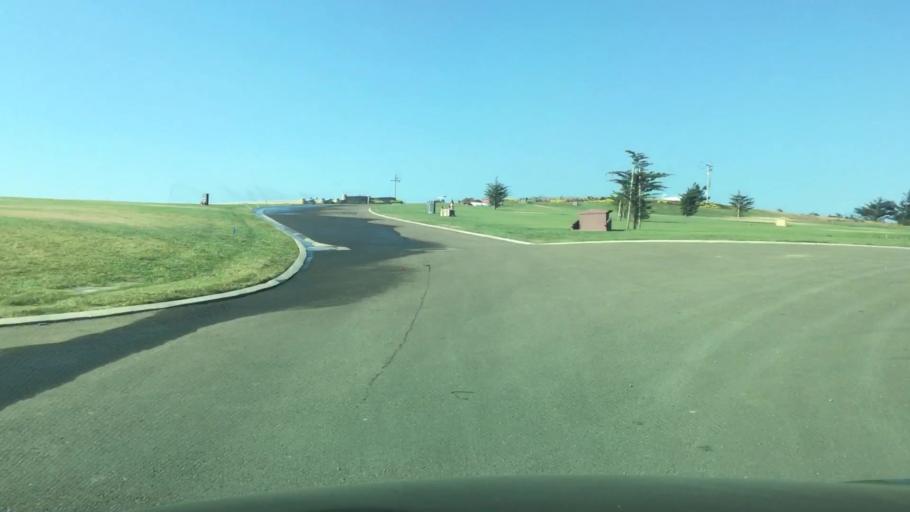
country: US
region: California
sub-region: San Mateo County
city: Highlands-Baywood Park
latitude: 37.5029
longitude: -122.3724
